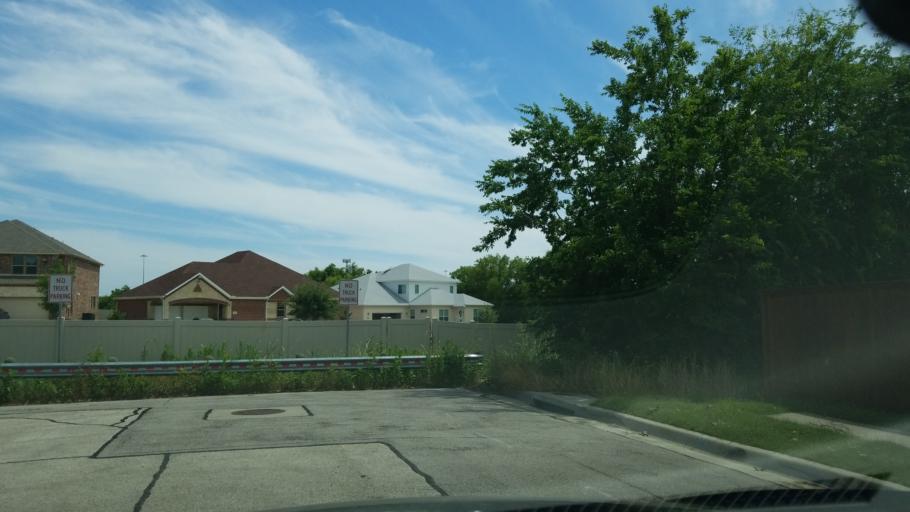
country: US
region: Texas
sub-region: Dallas County
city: Irving
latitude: 32.8736
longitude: -96.9991
